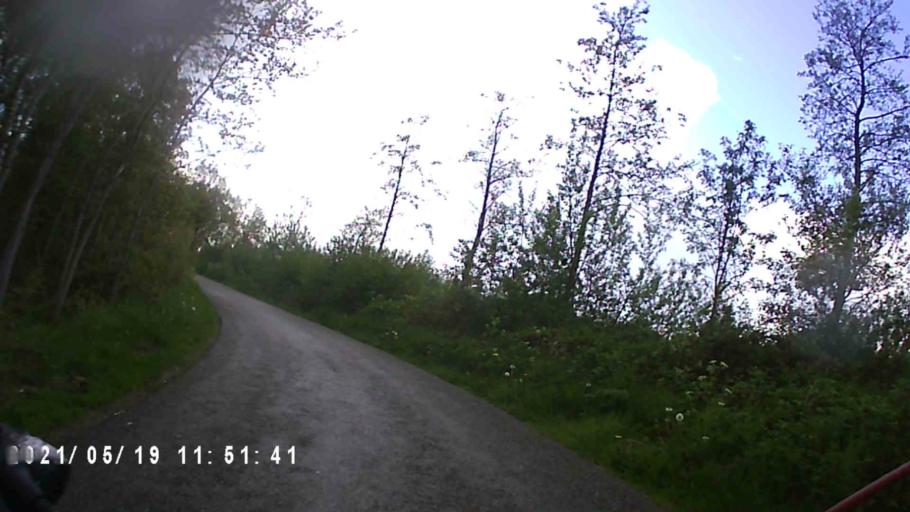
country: NL
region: Friesland
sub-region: Gemeente Kollumerland en Nieuwkruisland
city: Kollum
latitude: 53.2682
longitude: 6.1420
